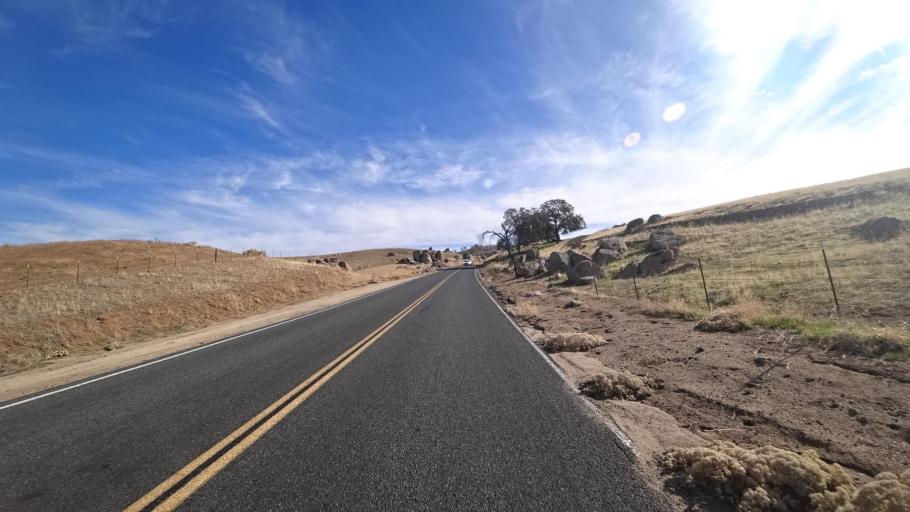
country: US
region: California
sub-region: Kern County
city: Oildale
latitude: 35.6121
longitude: -118.8631
